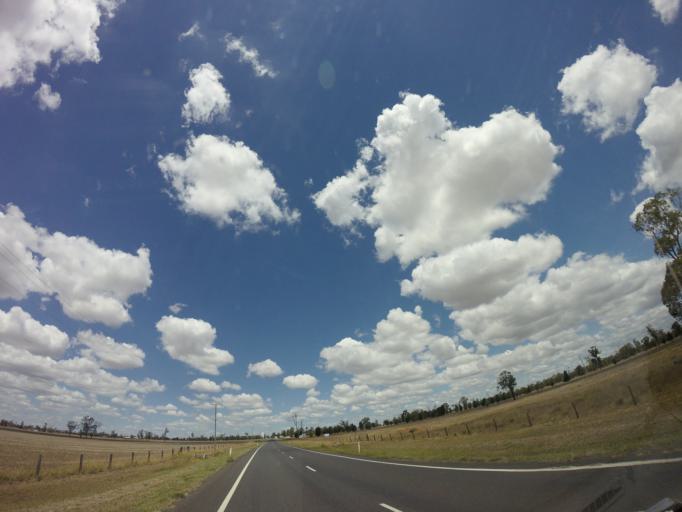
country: AU
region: Queensland
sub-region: Toowoomba
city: Oakey
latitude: -27.8740
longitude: 151.2468
